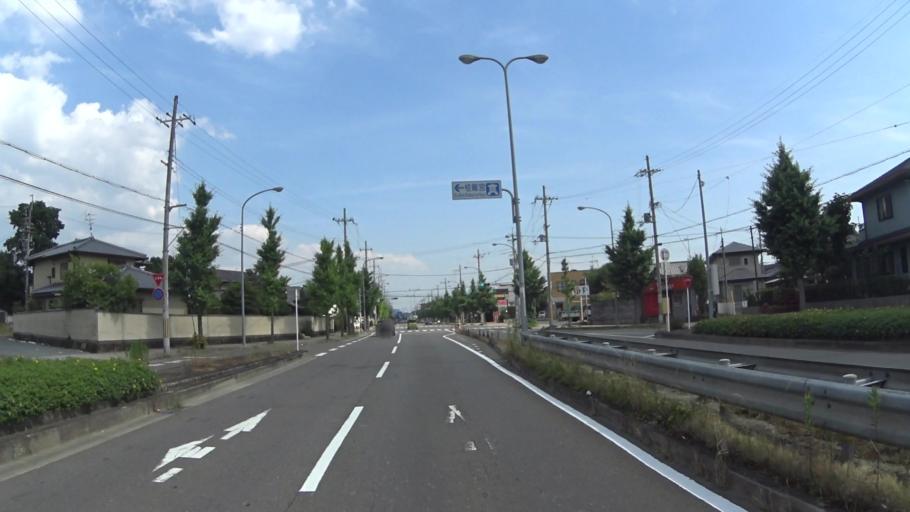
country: JP
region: Kyoto
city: Muko
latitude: 34.9859
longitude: 135.7065
